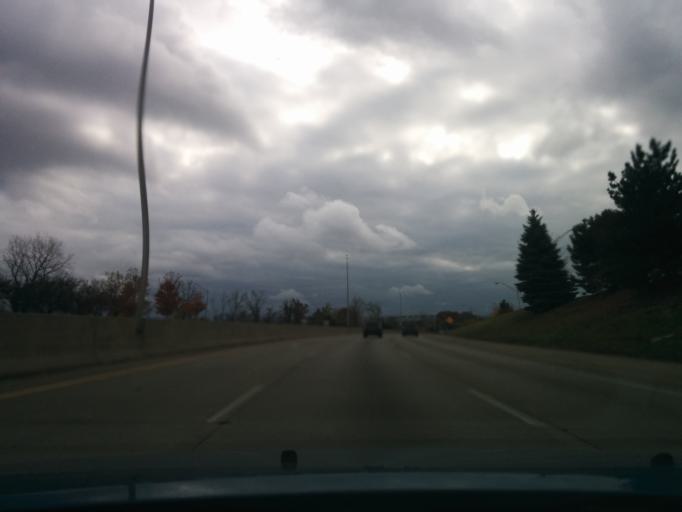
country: US
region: Michigan
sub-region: Wayne County
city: Melvindale
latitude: 42.2976
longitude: -83.2055
